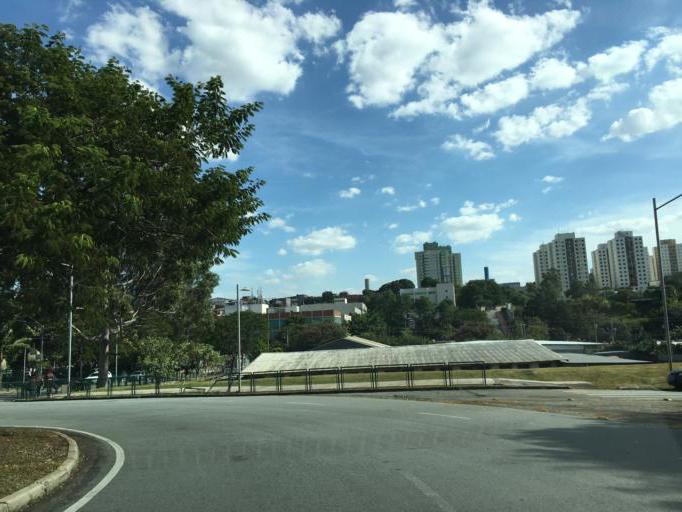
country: BR
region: Sao Paulo
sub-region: Osasco
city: Osasco
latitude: -23.5682
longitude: -46.7403
